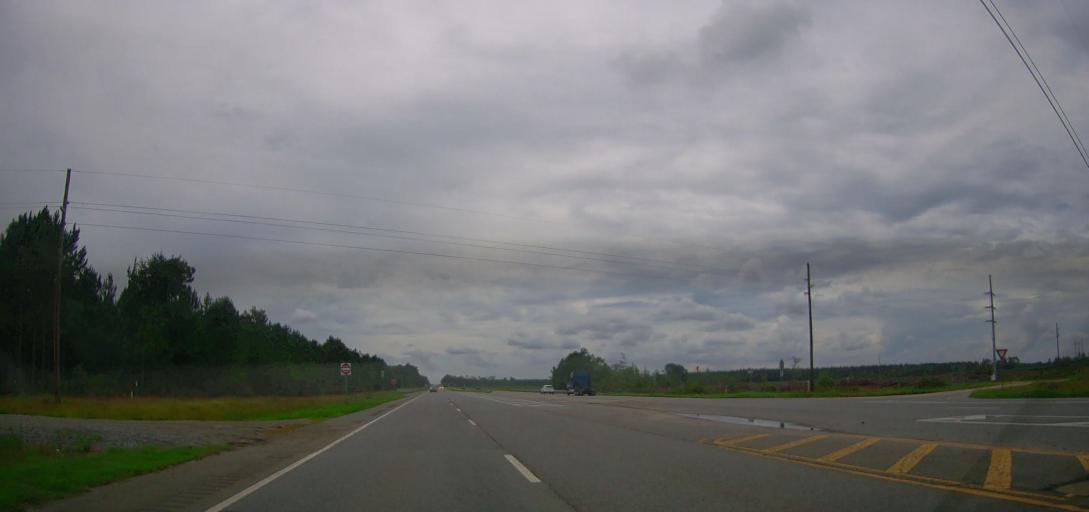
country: US
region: Georgia
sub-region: Appling County
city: Baxley
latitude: 31.7556
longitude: -82.2827
